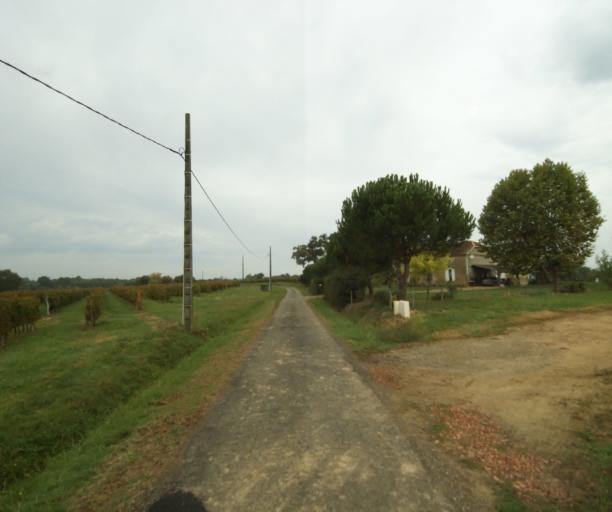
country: FR
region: Midi-Pyrenees
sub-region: Departement du Gers
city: Cazaubon
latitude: 43.9218
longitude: -0.1321
